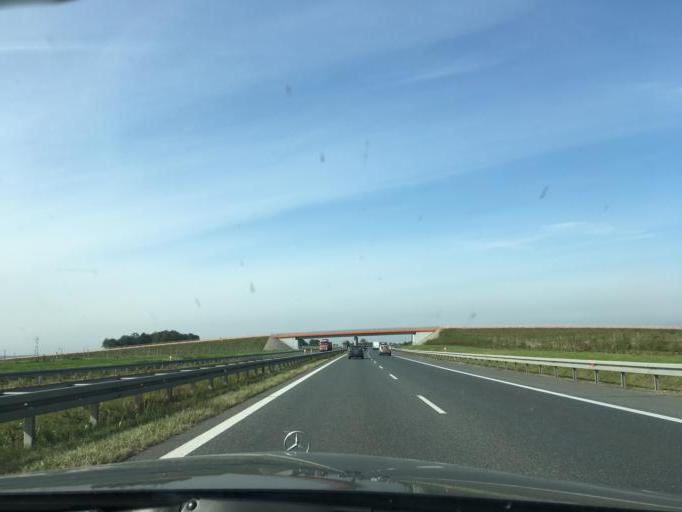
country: PL
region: Lower Silesian Voivodeship
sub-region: Powiat olesnicki
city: Dobroszyce
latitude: 51.2218
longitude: 17.3227
